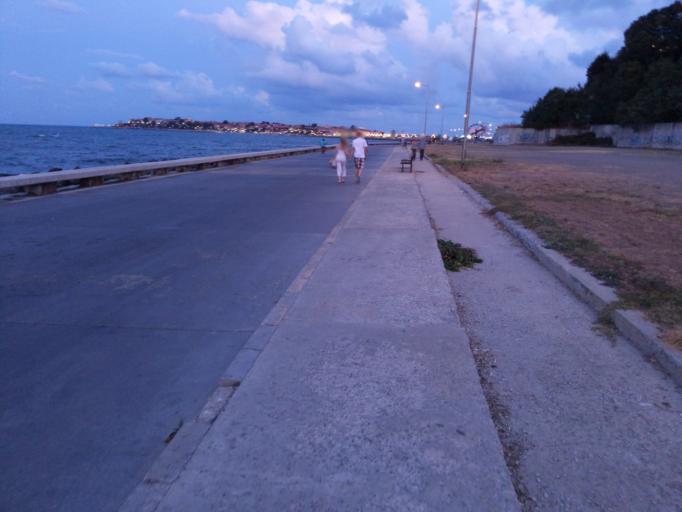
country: BG
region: Burgas
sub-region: Obshtina Nesebur
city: Nesebar
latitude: 42.6643
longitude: 27.7204
